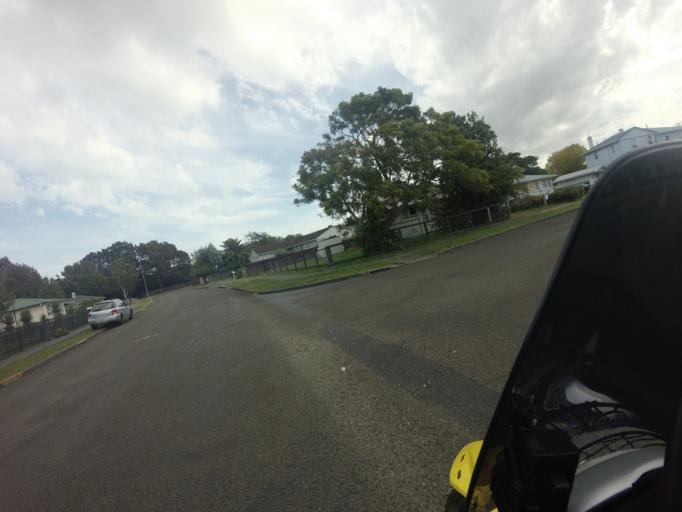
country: NZ
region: Gisborne
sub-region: Gisborne District
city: Gisborne
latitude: -38.6734
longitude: 178.0521
